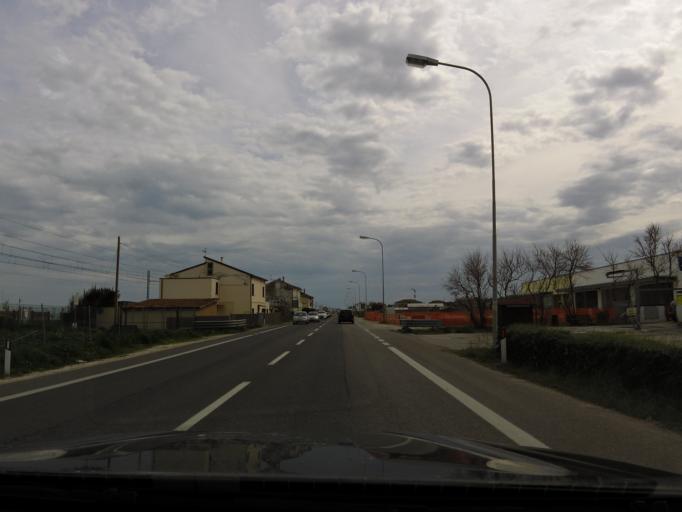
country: IT
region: The Marches
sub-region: Provincia di Macerata
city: Porto Potenza Picena
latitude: 43.3423
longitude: 13.7060
